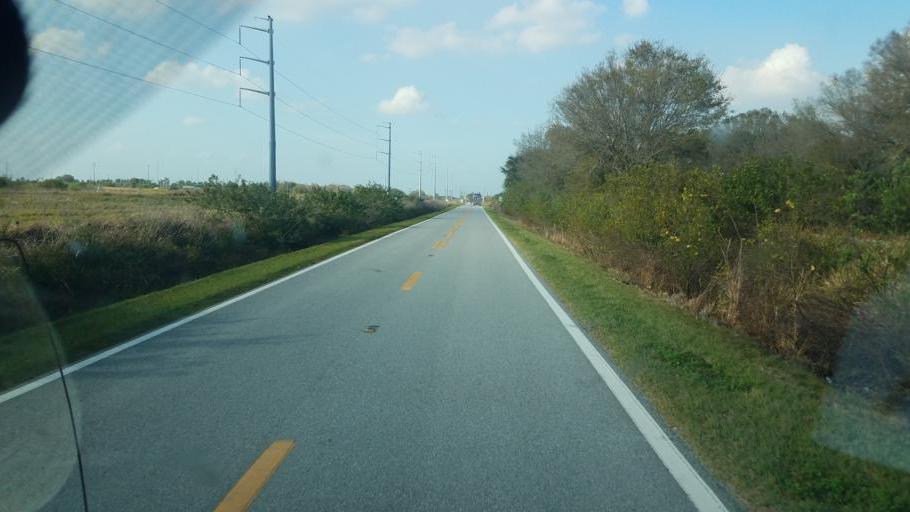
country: US
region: Florida
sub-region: Hardee County
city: Bowling Green
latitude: 27.6808
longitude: -81.9551
